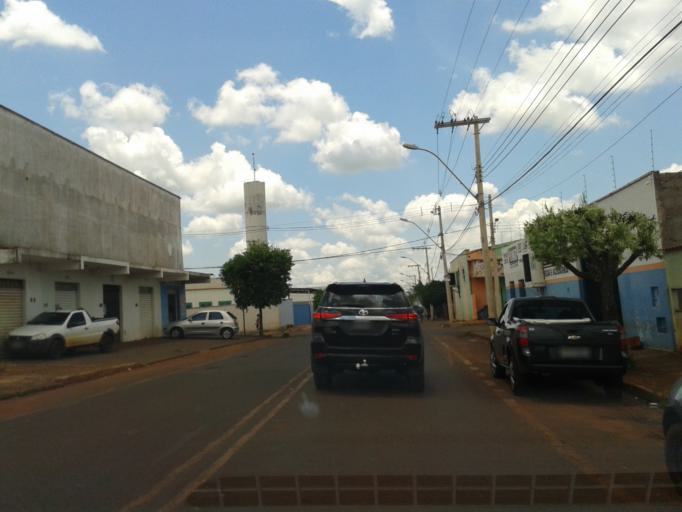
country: BR
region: Minas Gerais
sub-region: Centralina
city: Centralina
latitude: -18.7283
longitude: -49.1987
